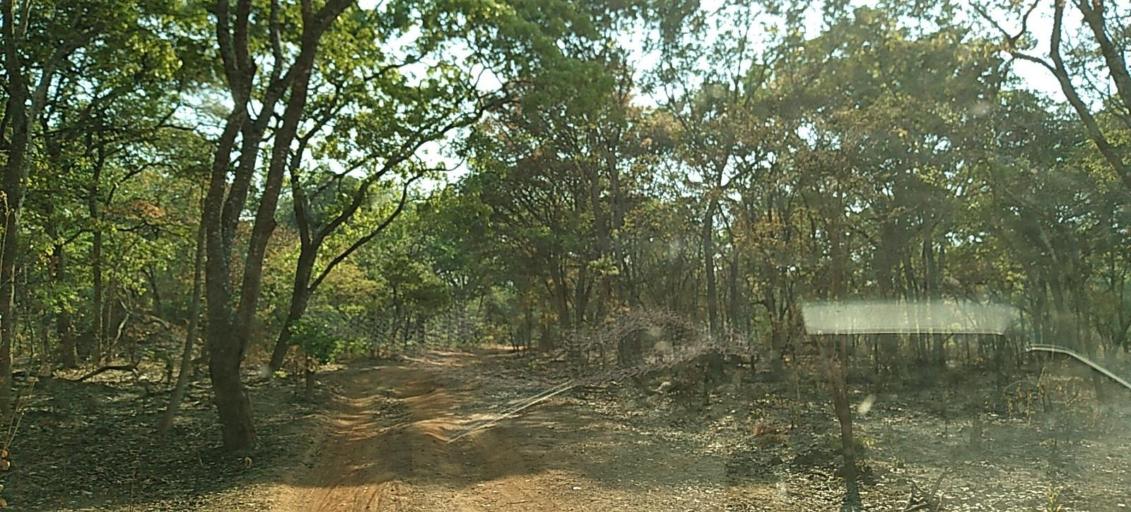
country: ZM
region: Copperbelt
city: Kalulushi
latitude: -13.0059
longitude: 27.7426
